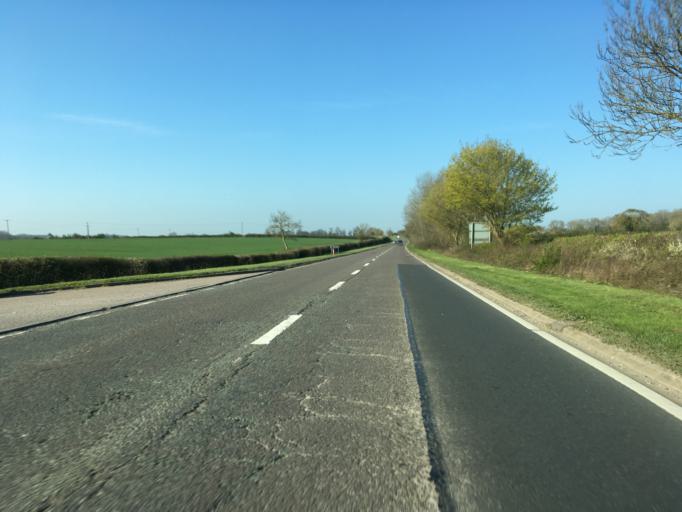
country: GB
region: England
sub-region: Northamptonshire
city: Deanshanger
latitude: 52.0365
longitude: -0.8961
